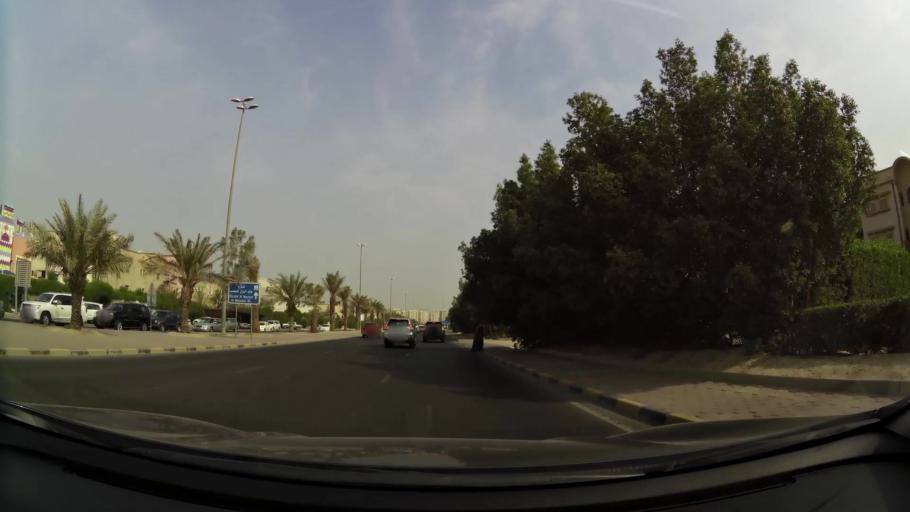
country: KW
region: Al Asimah
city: Ar Rabiyah
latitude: 29.2799
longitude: 47.9393
